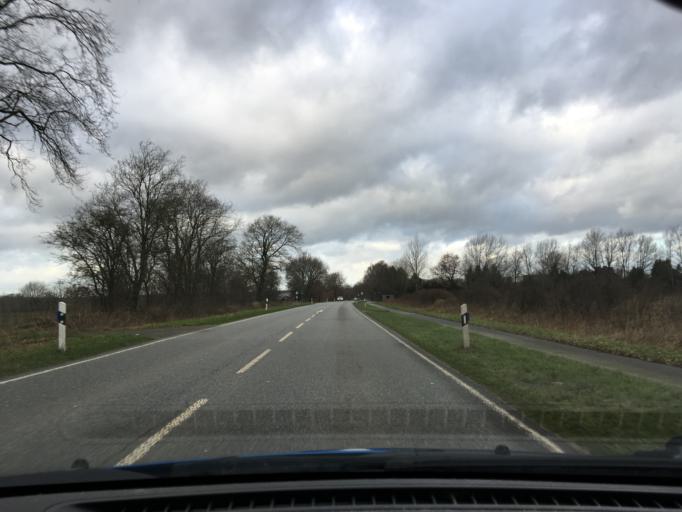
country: DE
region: Schleswig-Holstein
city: Ottenbuttel
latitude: 53.9894
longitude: 9.4938
